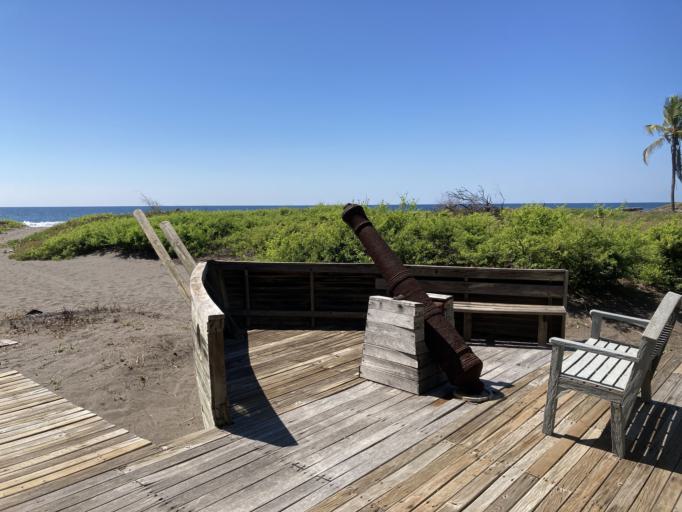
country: GT
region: Jutiapa
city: Pasaco
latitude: 13.8082
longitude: -90.2797
